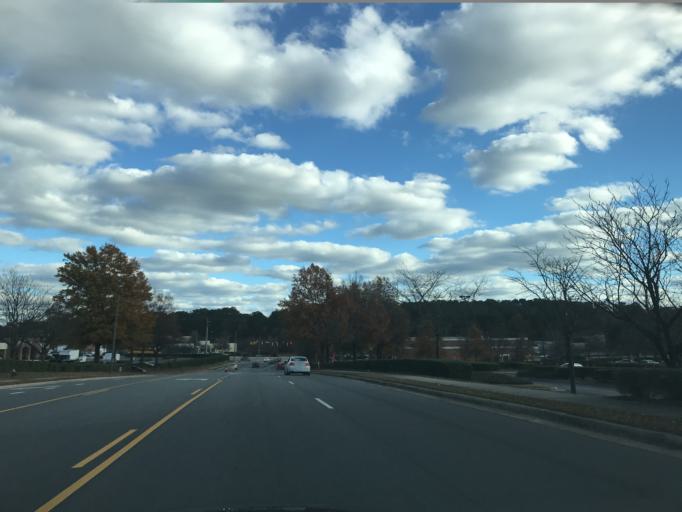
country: US
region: North Carolina
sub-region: Wake County
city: Raleigh
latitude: 35.8362
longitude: -78.5848
